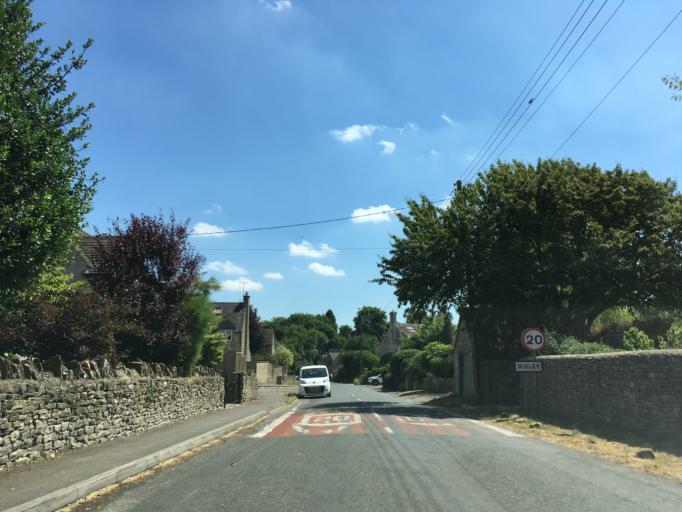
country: GB
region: England
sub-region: Gloucestershire
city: Chalford
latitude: 51.7542
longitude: -2.1432
